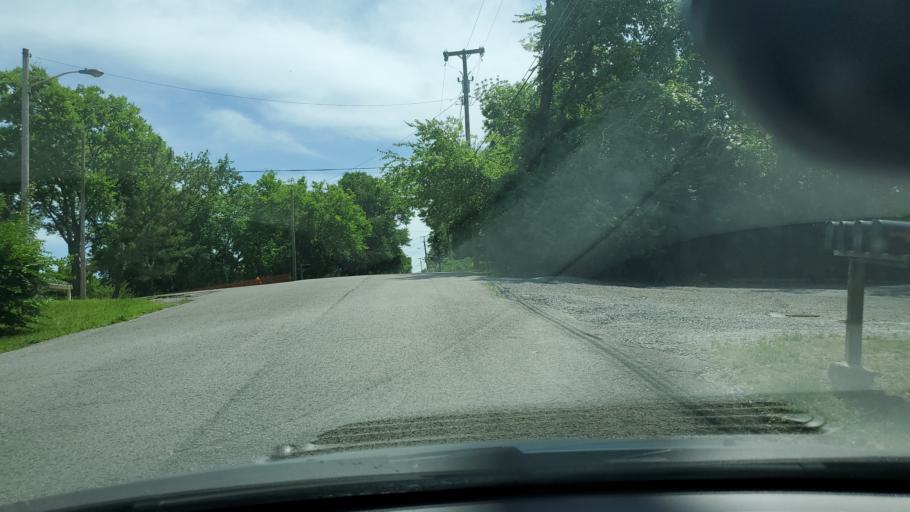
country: US
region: Tennessee
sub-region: Davidson County
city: Nashville
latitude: 36.2242
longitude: -86.7391
